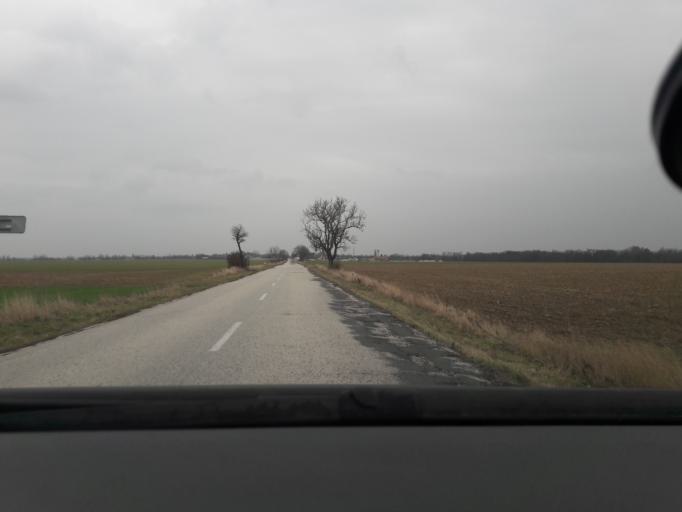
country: SK
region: Bratislavsky
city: Senec
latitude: 48.3239
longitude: 17.4341
